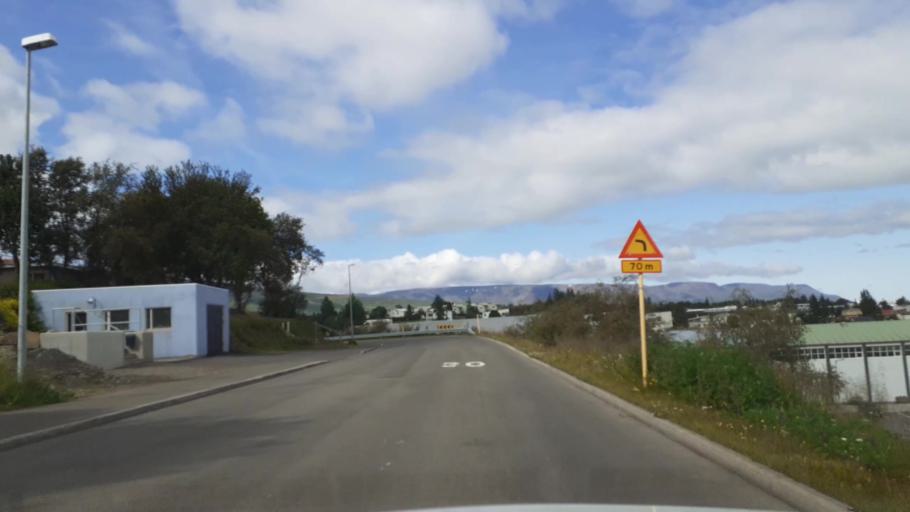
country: IS
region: Northeast
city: Akureyri
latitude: 65.6861
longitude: -18.1058
